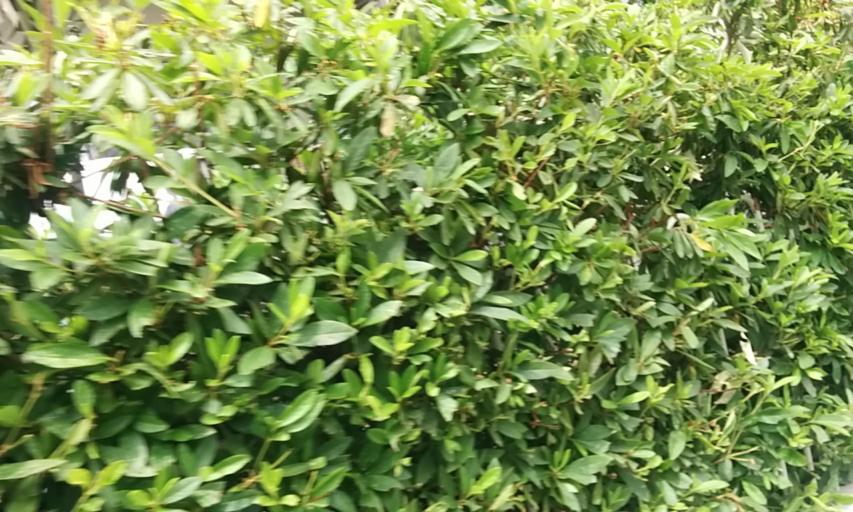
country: JP
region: Tokyo
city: Tokyo
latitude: 35.7170
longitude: 139.7026
